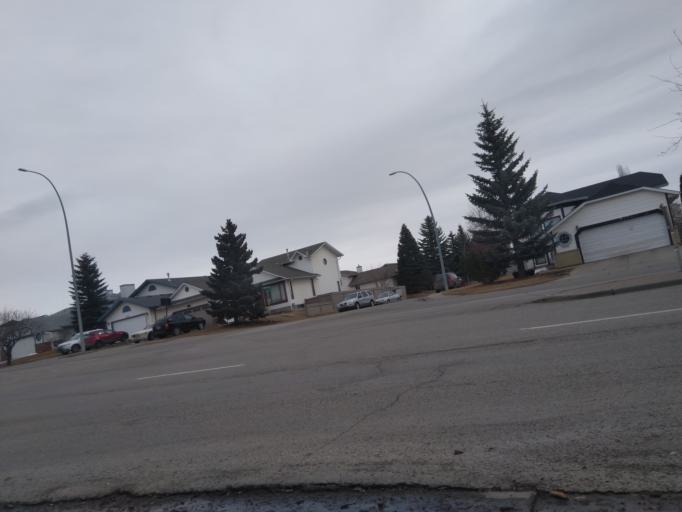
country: CA
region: Alberta
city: Calgary
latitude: 51.1555
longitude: -114.0426
